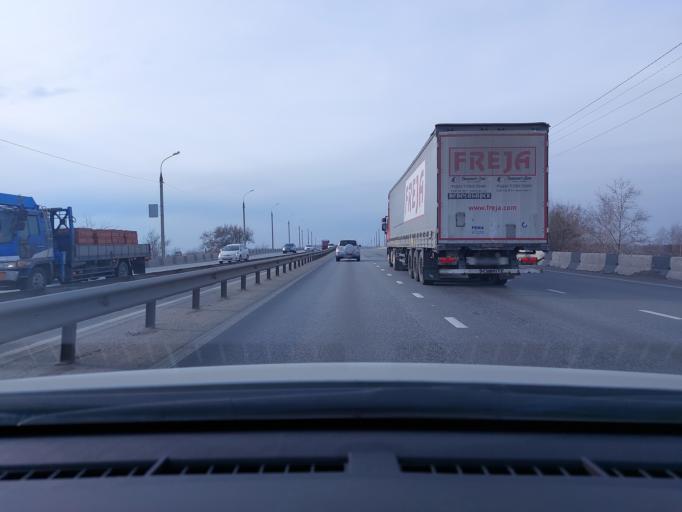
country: RU
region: Irkutsk
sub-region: Irkutskiy Rayon
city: Irkutsk
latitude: 52.3252
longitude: 104.2296
